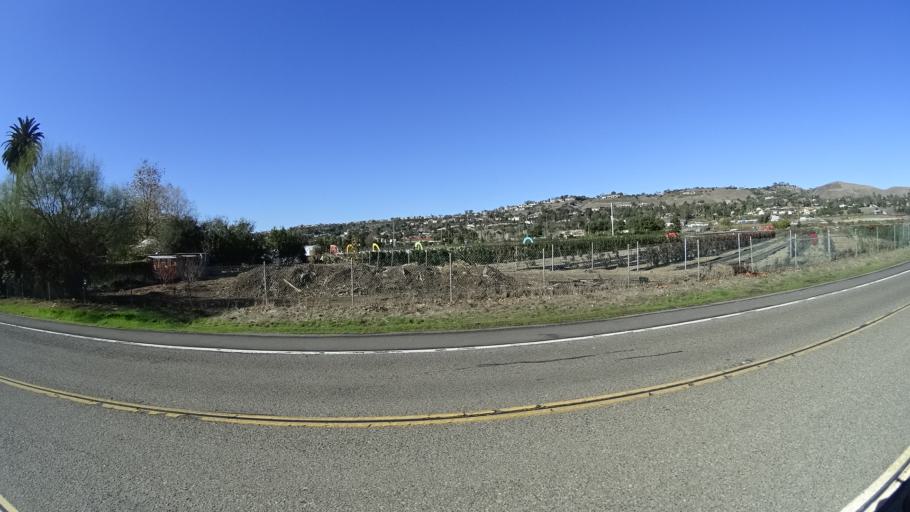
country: US
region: California
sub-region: Orange County
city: San Juan Capistrano
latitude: 33.4885
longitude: -117.6722
